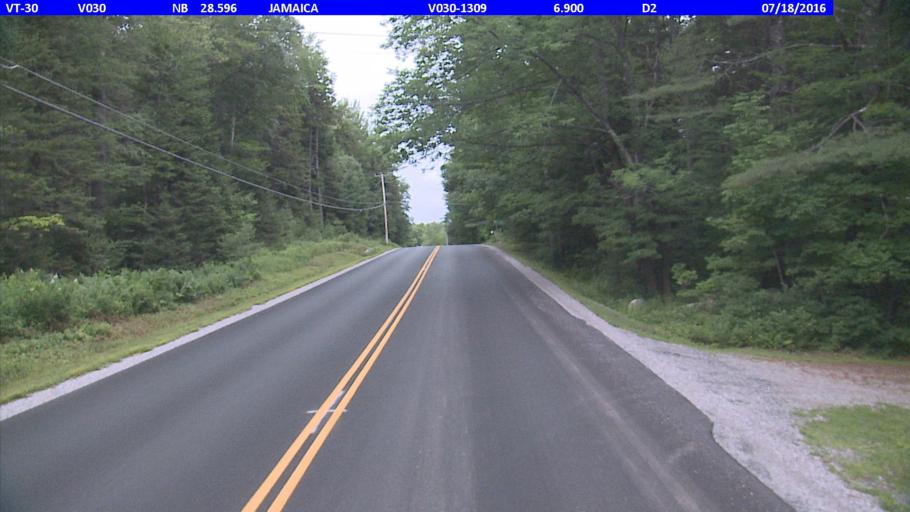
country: US
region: Vermont
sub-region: Windham County
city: Dover
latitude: 43.1297
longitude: -72.8135
